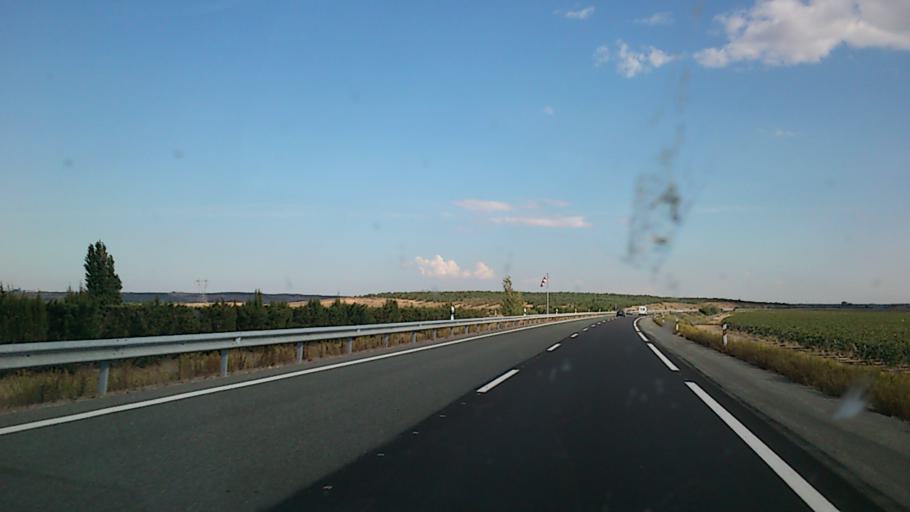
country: ES
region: Navarre
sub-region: Provincia de Navarra
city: Corella
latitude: 42.1506
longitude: -1.7969
